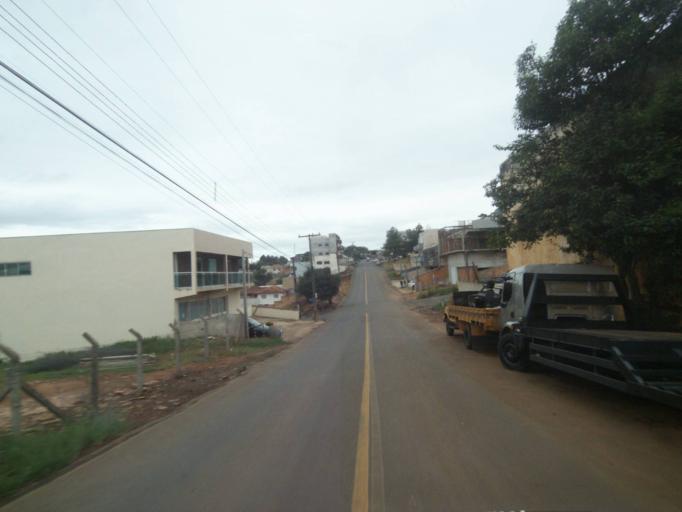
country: BR
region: Parana
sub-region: Telemaco Borba
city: Telemaco Borba
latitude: -24.3316
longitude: -50.6446
